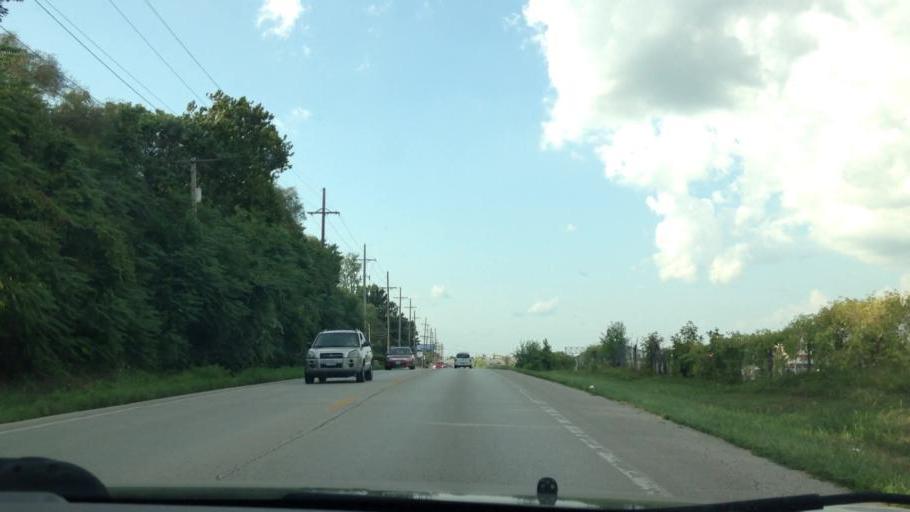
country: US
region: Missouri
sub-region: Platte County
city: Weatherby Lake
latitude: 39.2372
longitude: -94.6589
